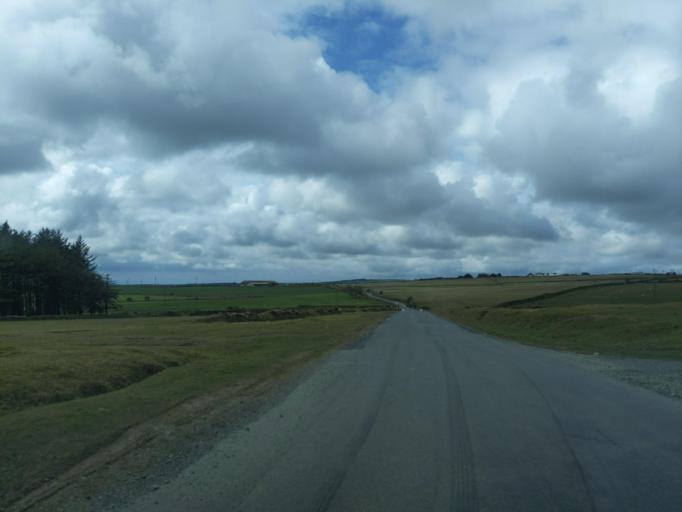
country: GB
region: England
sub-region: Cornwall
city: Camelford
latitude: 50.6397
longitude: -4.6301
